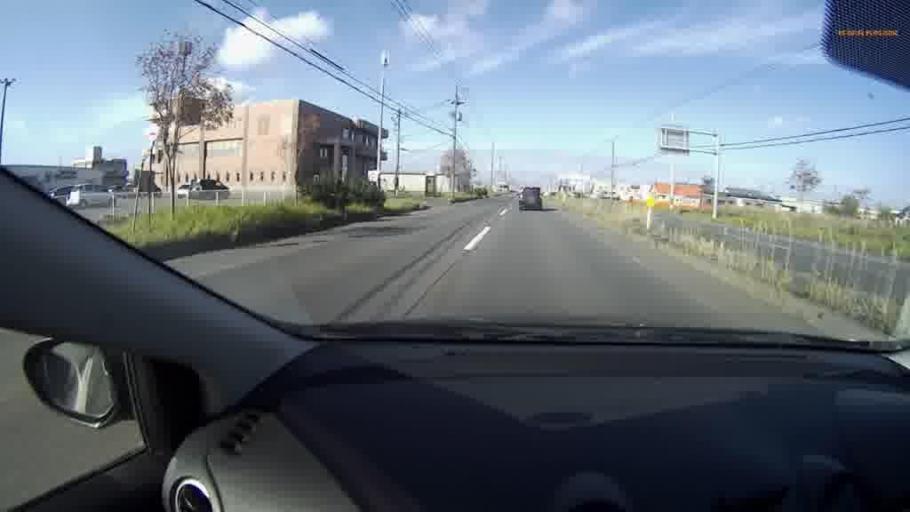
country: JP
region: Hokkaido
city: Kushiro
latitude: 42.9968
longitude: 144.4335
